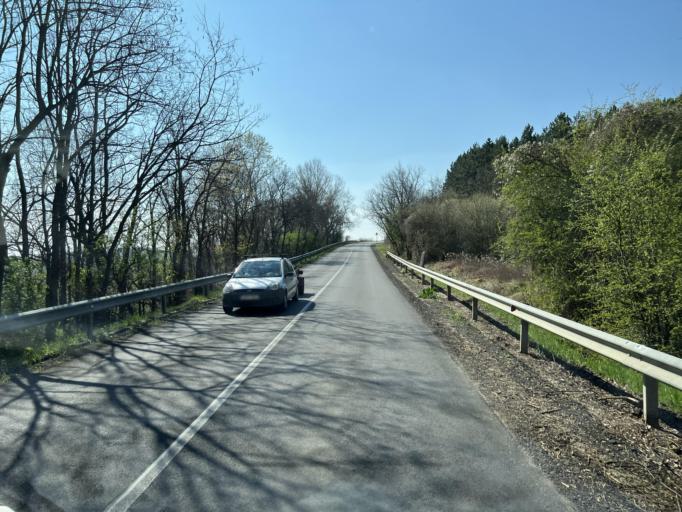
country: HU
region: Pest
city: Orbottyan
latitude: 47.7297
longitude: 19.2692
